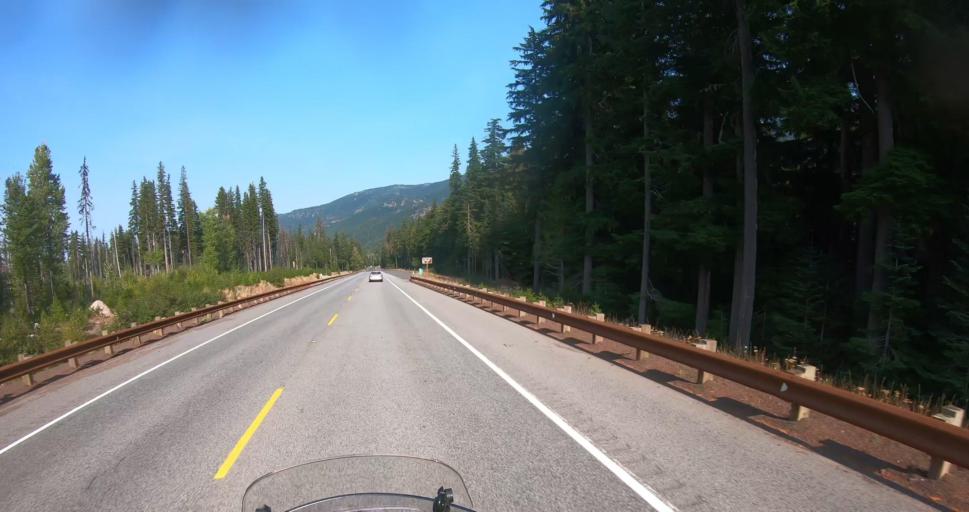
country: US
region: Oregon
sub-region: Hood River County
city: Odell
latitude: 45.3268
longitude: -121.5898
